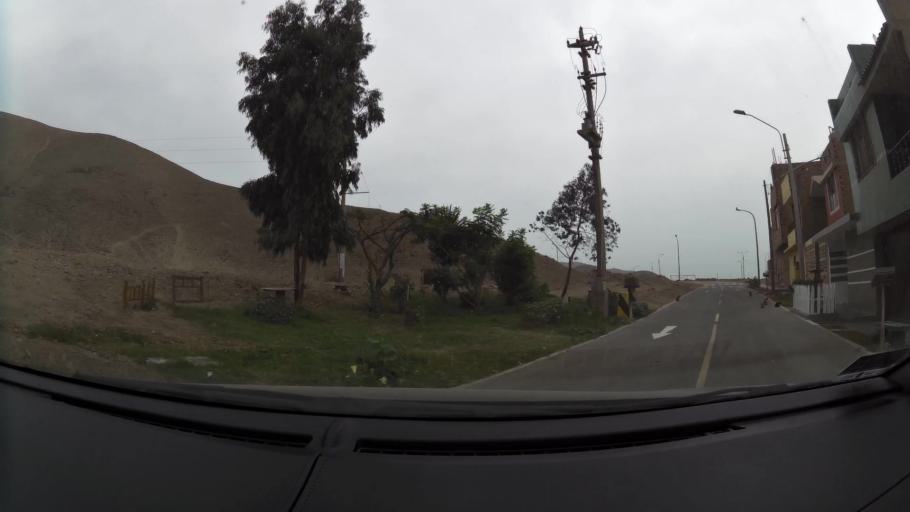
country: PE
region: Lima
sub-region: Lima
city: Santa Rosa
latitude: -11.7912
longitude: -77.1540
